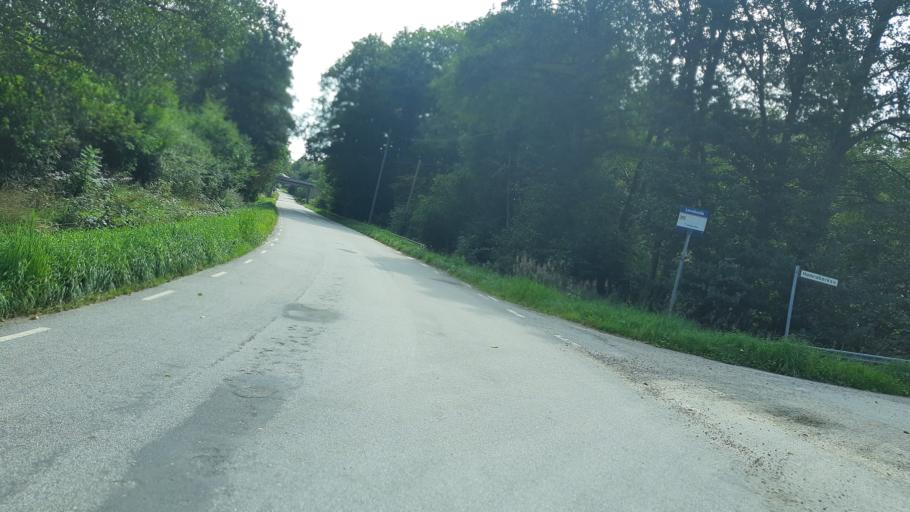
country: SE
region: Blekinge
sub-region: Ronneby Kommun
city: Kallinge
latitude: 56.2062
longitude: 15.3419
